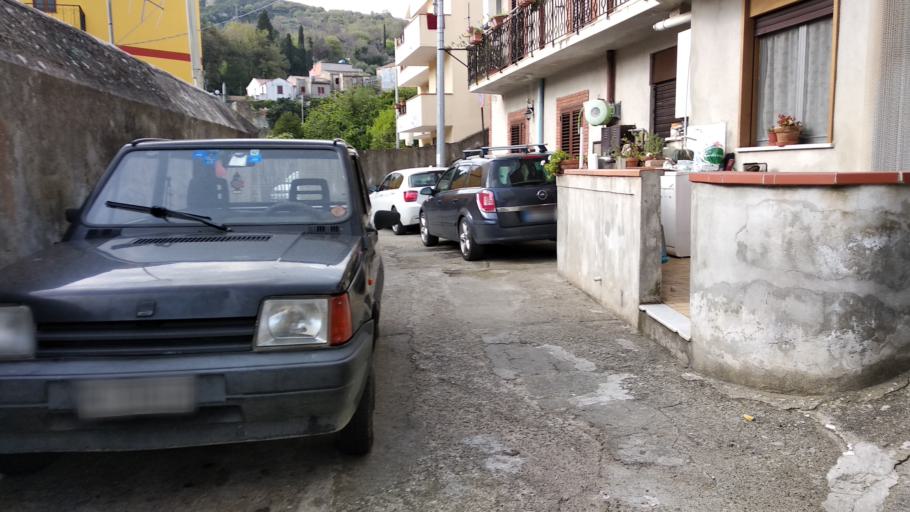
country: IT
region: Sicily
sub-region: Messina
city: Villafranca Tirrena
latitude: 38.2231
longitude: 15.4515
